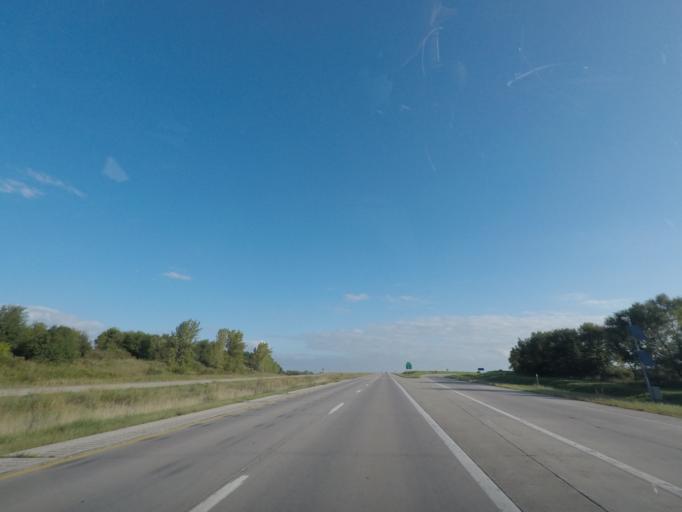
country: US
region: Iowa
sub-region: Warren County
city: Carlisle
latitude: 41.5191
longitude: -93.5197
